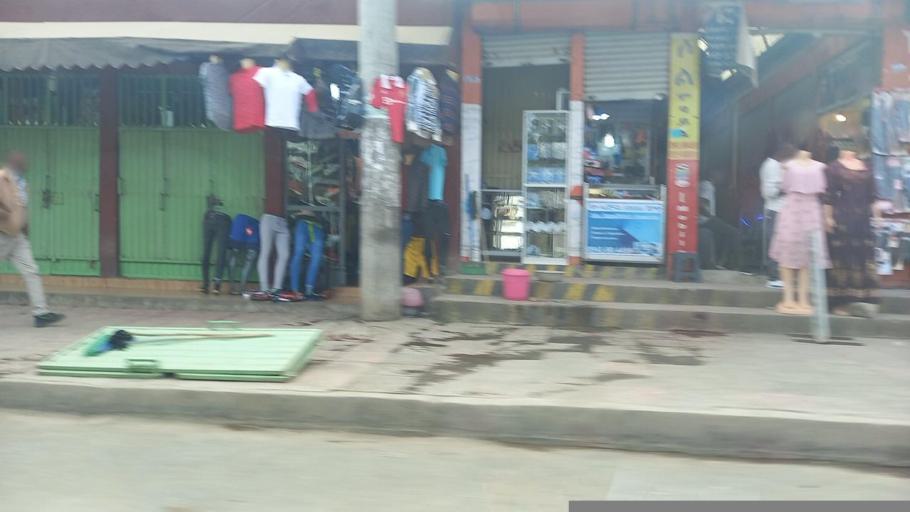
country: ET
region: Adis Abeba
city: Addis Ababa
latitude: 9.0179
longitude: 38.8238
